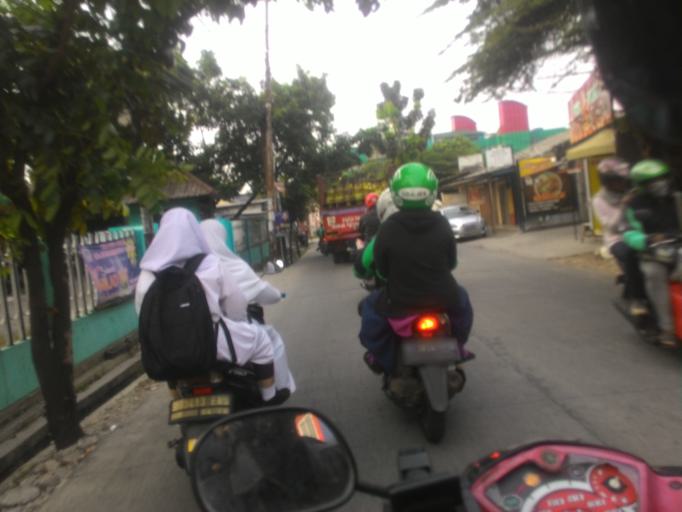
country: ID
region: West Java
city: Depok
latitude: -6.3725
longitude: 106.8133
